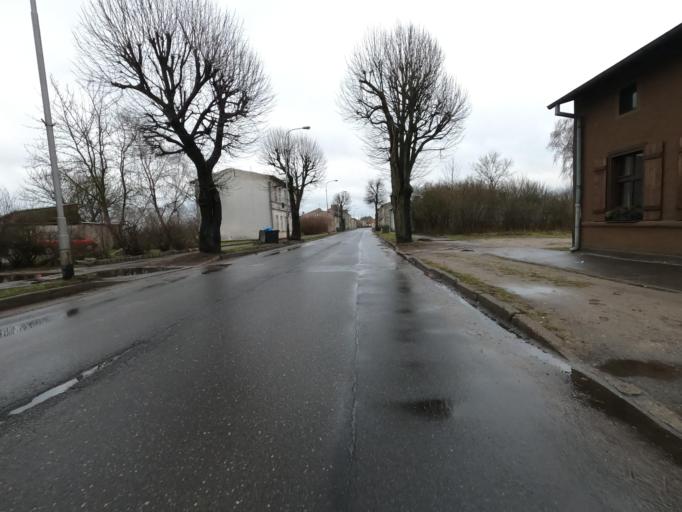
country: PL
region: Greater Poland Voivodeship
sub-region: Powiat pilski
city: Pila
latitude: 53.1429
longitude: 16.7580
